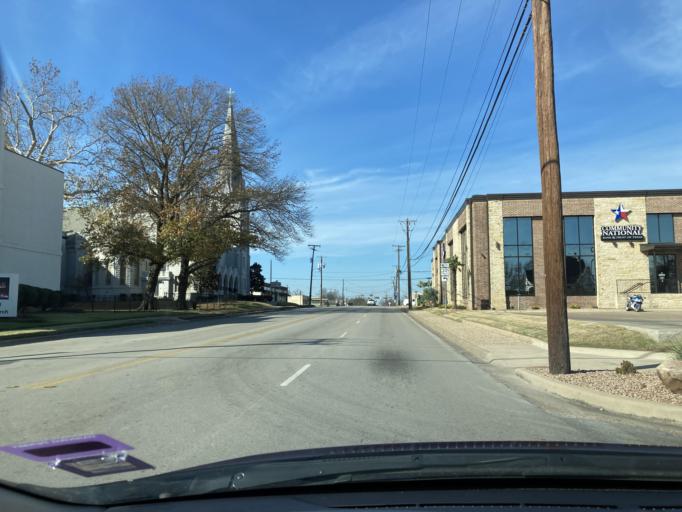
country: US
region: Texas
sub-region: Navarro County
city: Corsicana
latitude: 32.0927
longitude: -96.4703
